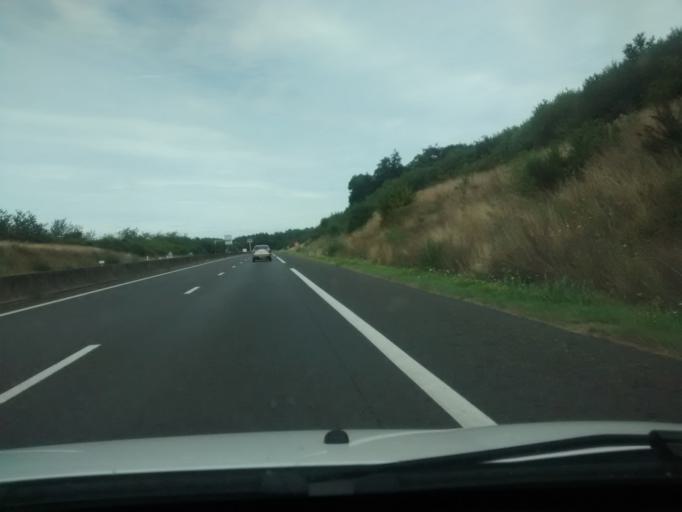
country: FR
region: Brittany
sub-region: Departement d'Ille-et-Vilaine
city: Saint-Etienne-en-Cogles
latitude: 48.3975
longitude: -1.3090
